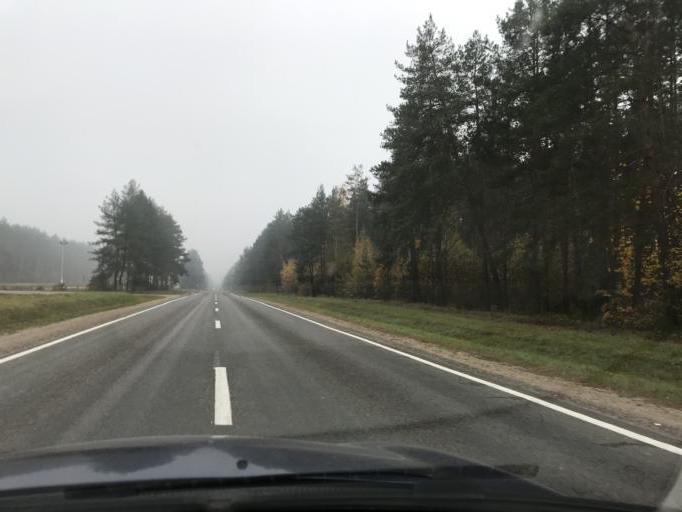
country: BY
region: Grodnenskaya
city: Hrodna
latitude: 53.7999
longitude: 23.8580
